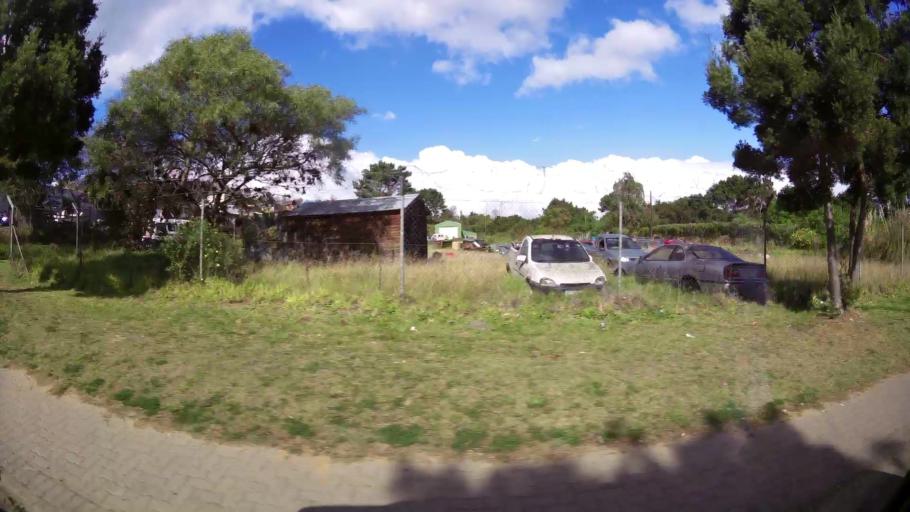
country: ZA
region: Western Cape
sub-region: Eden District Municipality
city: Knysna
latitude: -34.0481
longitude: 23.0817
